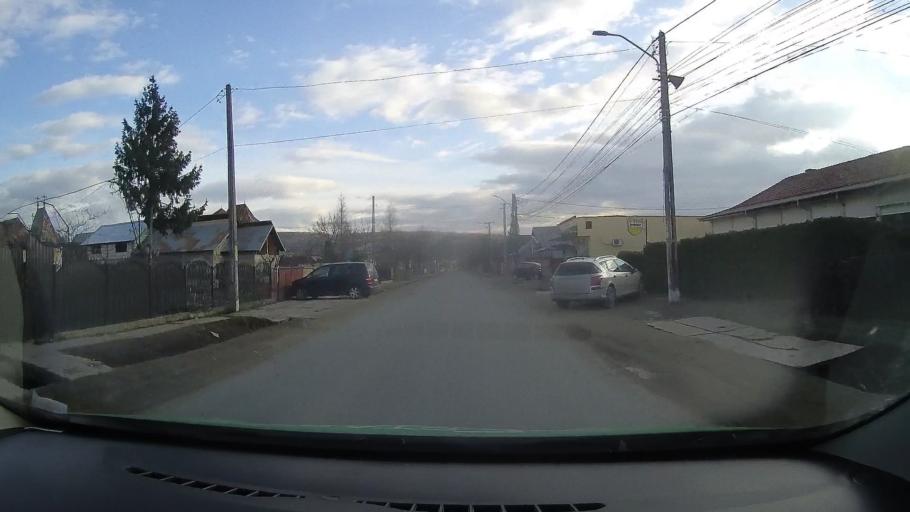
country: RO
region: Dambovita
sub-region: Comuna Ocnita
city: Ocnita
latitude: 44.9809
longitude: 25.5557
